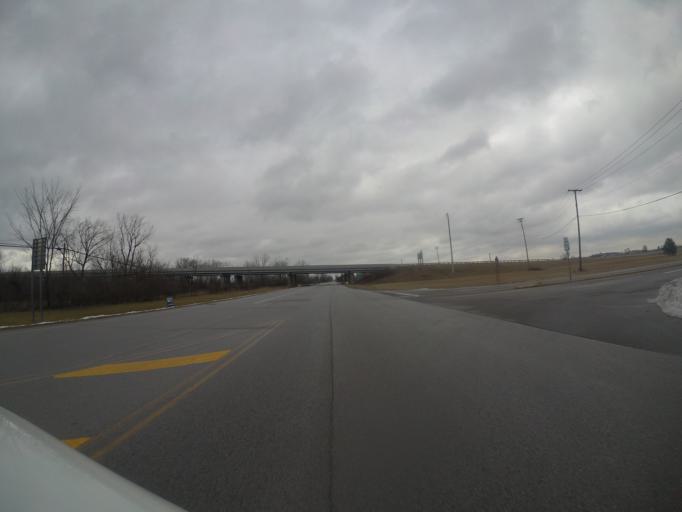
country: US
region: Ohio
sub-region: Wood County
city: Walbridge
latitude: 41.5631
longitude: -83.5118
